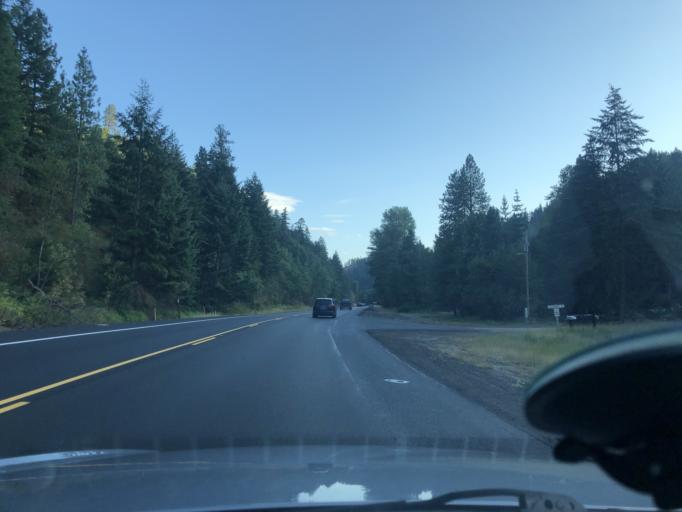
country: US
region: Washington
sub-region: Kittitas County
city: Cle Elum
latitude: 47.2261
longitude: -120.6955
